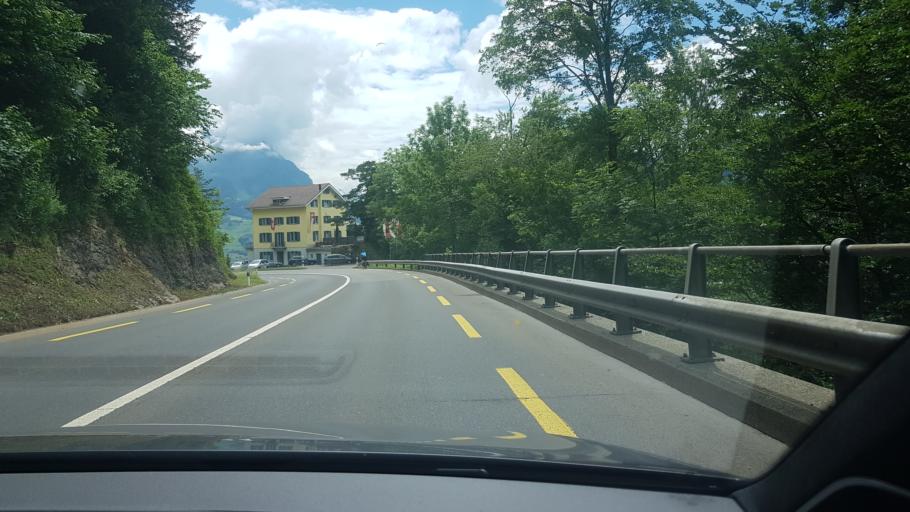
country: CH
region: Schwyz
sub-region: Bezirk Schwyz
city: Steinen
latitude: 47.0482
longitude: 8.6290
